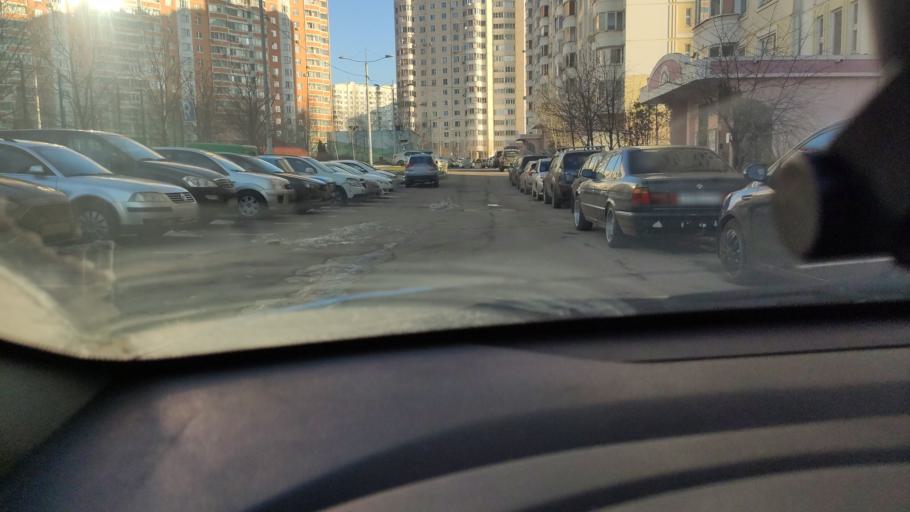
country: RU
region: Moskovskaya
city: Kommunarka
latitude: 55.5379
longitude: 37.5112
